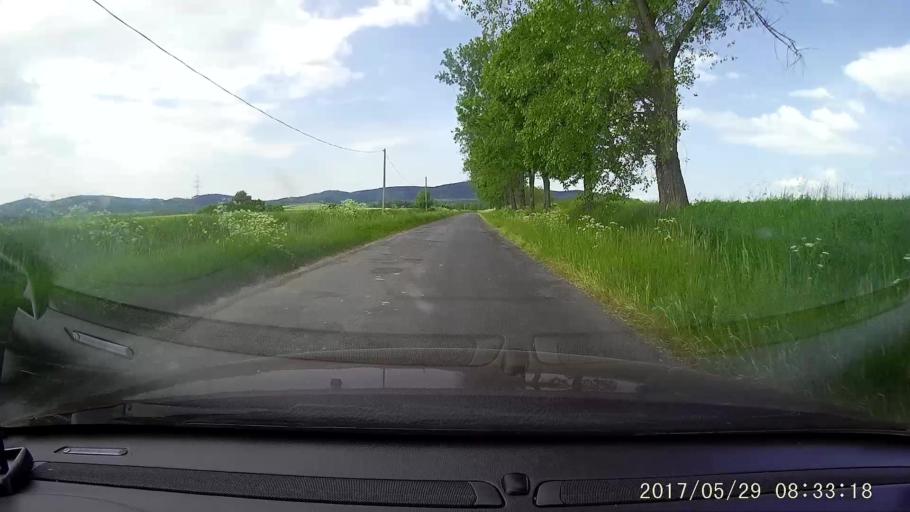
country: PL
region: Lower Silesian Voivodeship
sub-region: Powiat zlotoryjski
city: Swierzawa
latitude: 51.0145
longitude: 15.8738
